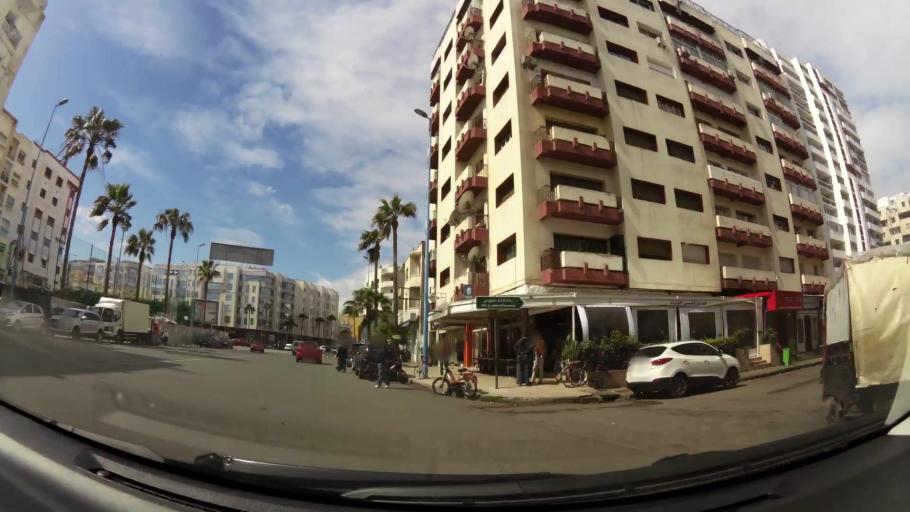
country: MA
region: Grand Casablanca
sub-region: Casablanca
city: Casablanca
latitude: 33.5833
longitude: -7.6404
